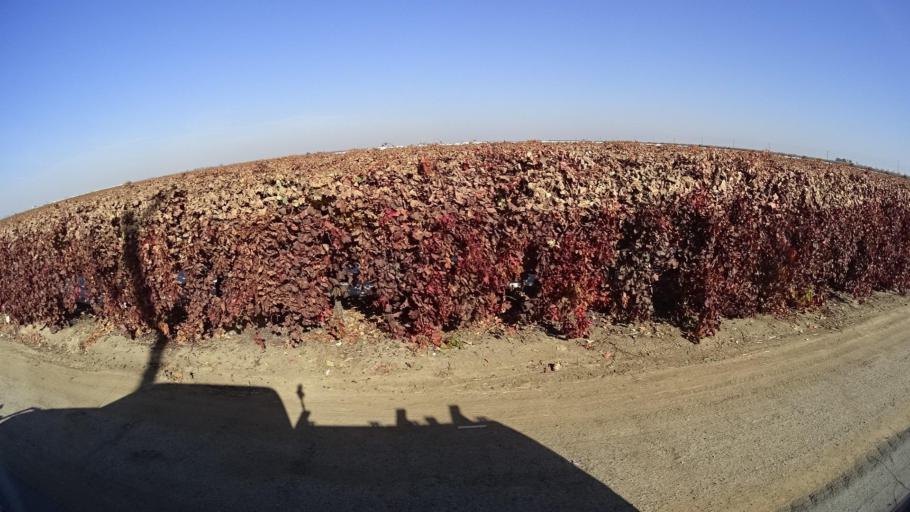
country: US
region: California
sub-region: Kern County
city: McFarland
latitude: 35.7179
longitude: -119.2093
